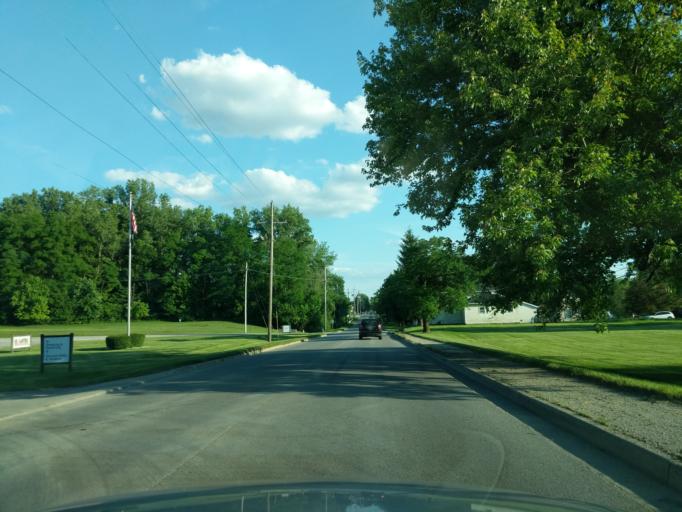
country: US
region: Indiana
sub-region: Huntington County
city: Huntington
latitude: 40.8864
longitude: -85.4712
